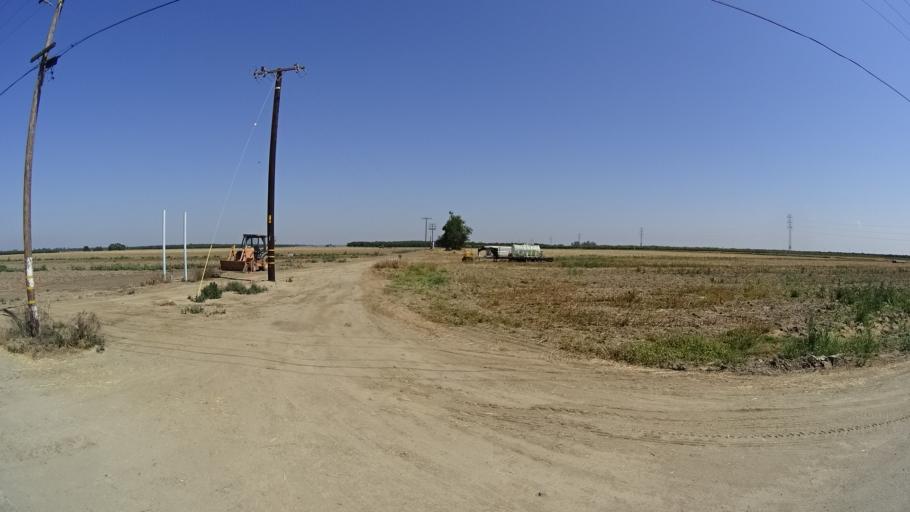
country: US
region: California
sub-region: Kings County
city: Hanford
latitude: 36.3716
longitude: -119.5940
